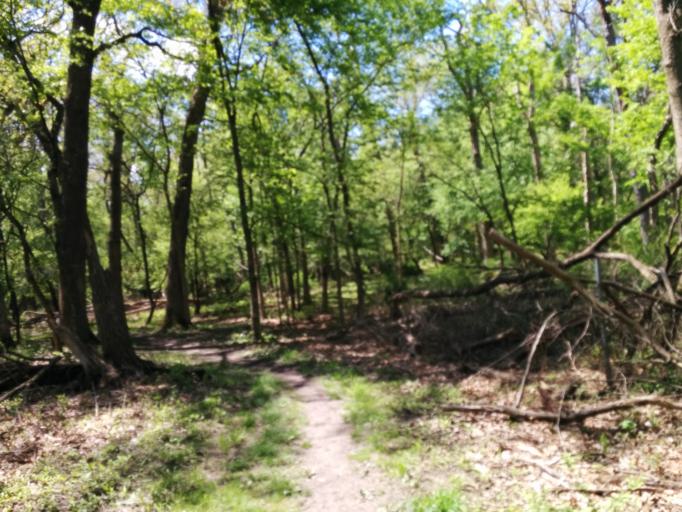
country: US
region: Illinois
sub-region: Cook County
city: Norridge
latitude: 41.9732
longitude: -87.8512
